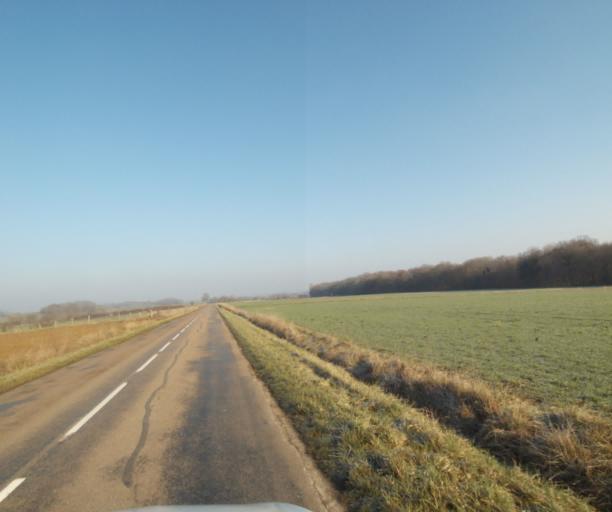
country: FR
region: Champagne-Ardenne
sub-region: Departement de la Haute-Marne
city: Montier-en-Der
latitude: 48.4361
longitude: 4.7547
